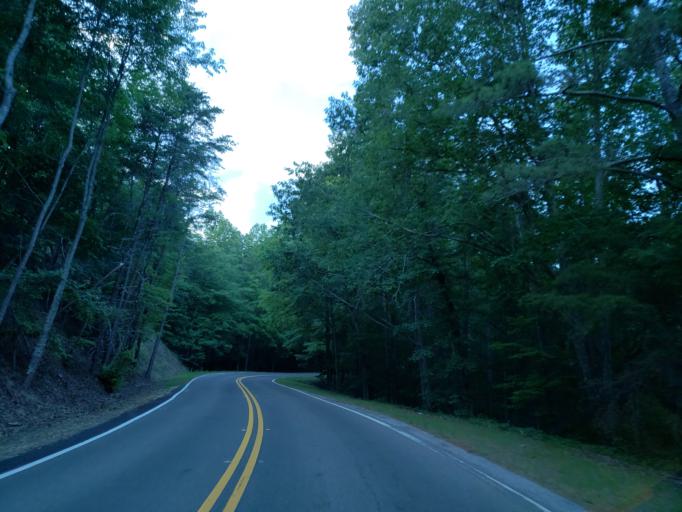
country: US
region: Georgia
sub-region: Bartow County
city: Emerson
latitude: 34.1846
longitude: -84.7397
